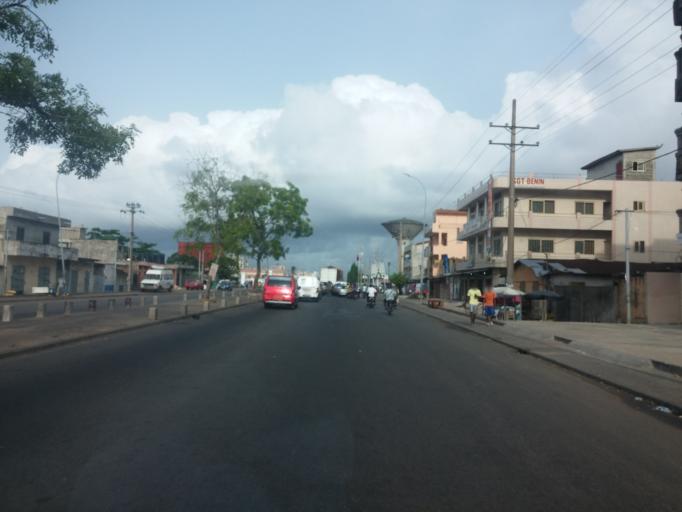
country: BJ
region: Littoral
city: Cotonou
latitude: 6.3770
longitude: 2.3913
